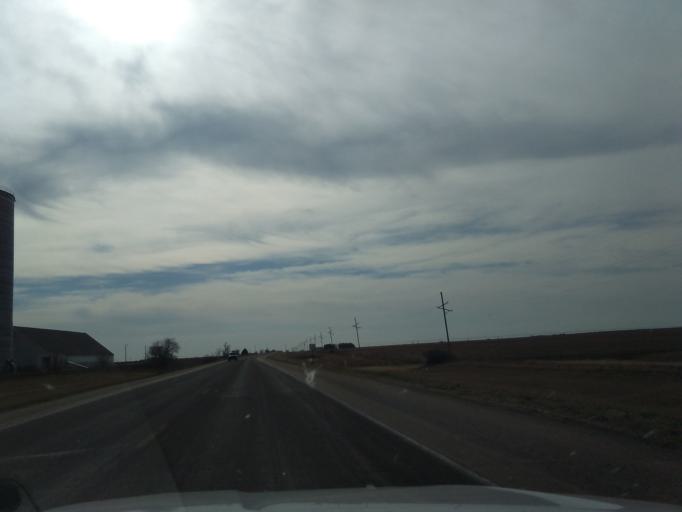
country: US
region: Nebraska
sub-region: Jefferson County
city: Fairbury
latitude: 40.1818
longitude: -97.0877
